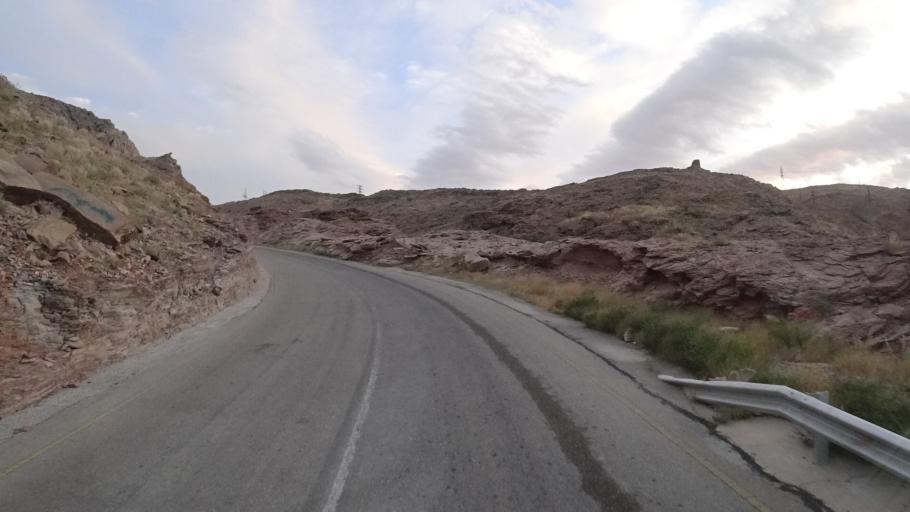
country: OM
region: Muhafazat Masqat
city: Muscat
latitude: 23.5753
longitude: 58.5497
